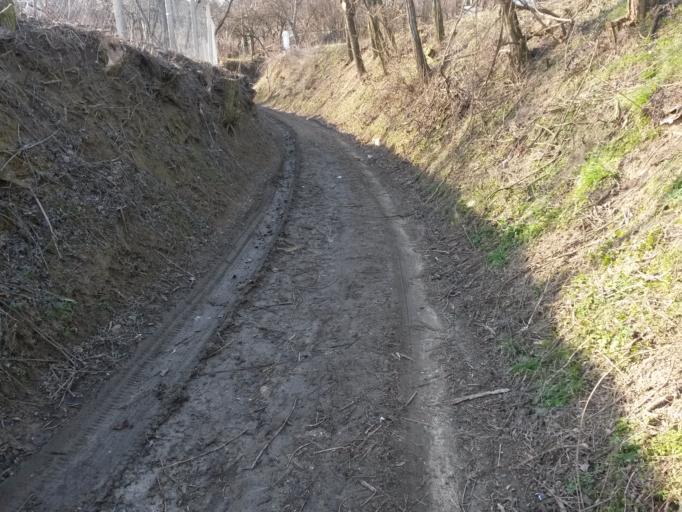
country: HU
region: Pest
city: Zsambek
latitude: 47.5501
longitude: 18.7104
